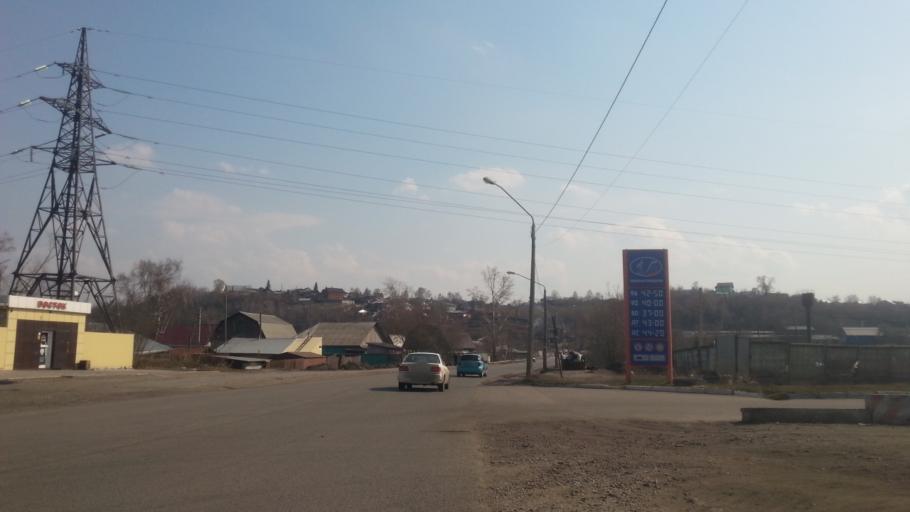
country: RU
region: Altai Krai
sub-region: Gorod Barnaulskiy
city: Barnaul
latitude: 53.3220
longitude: 83.7688
